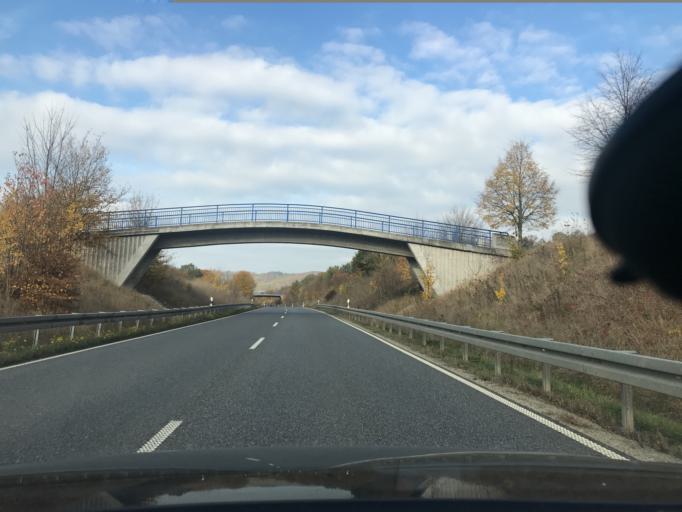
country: DE
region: Hesse
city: Wanfried
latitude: 51.1853
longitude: 10.1802
